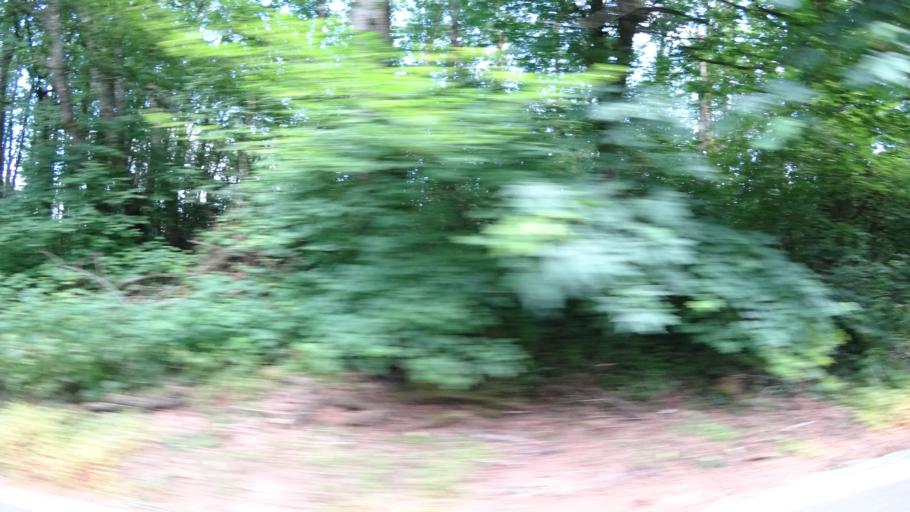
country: US
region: Oregon
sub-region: Washington County
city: Cedar Mill
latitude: 45.5746
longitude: -122.7943
